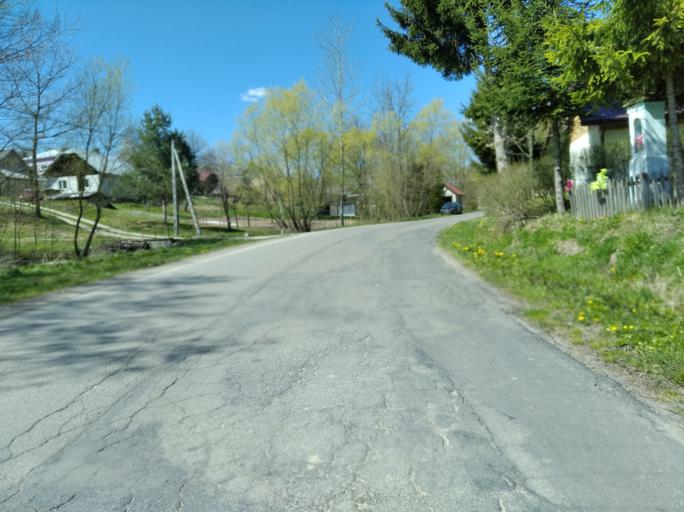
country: PL
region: Subcarpathian Voivodeship
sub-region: Powiat brzozowski
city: Jablonka
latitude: 49.7214
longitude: 22.1198
